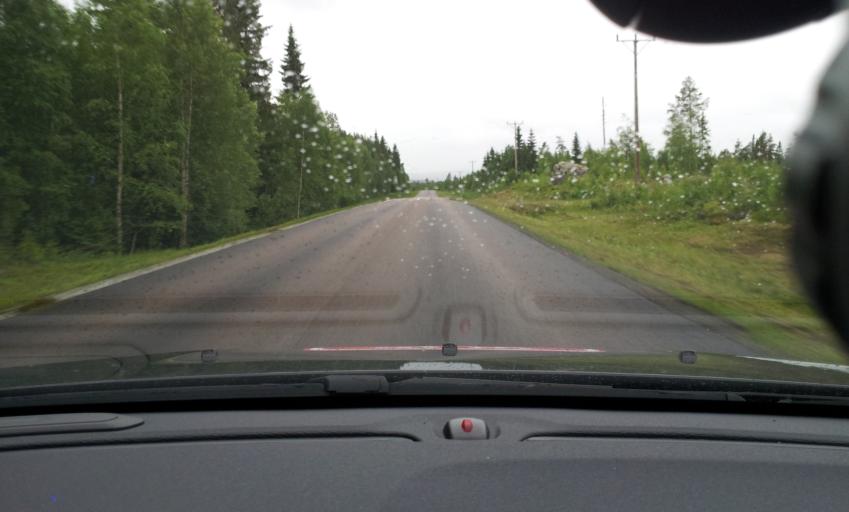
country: SE
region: Jaemtland
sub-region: Ragunda Kommun
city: Hammarstrand
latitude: 63.1985
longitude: 15.9428
